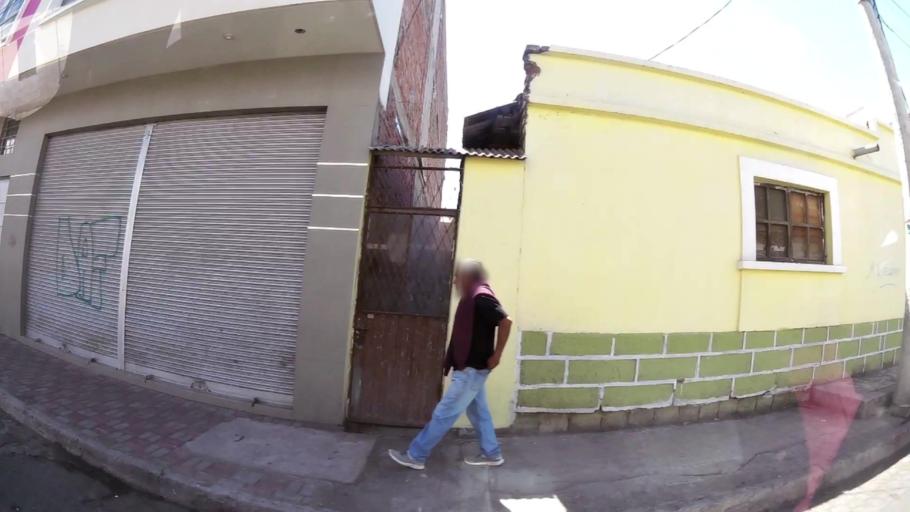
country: EC
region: Chimborazo
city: Riobamba
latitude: -1.6656
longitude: -78.6476
